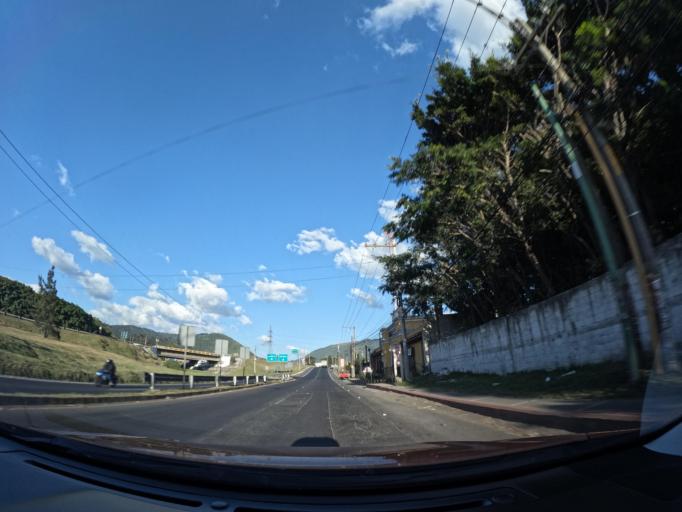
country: GT
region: Escuintla
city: Palin
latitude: 14.4098
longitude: -90.6836
